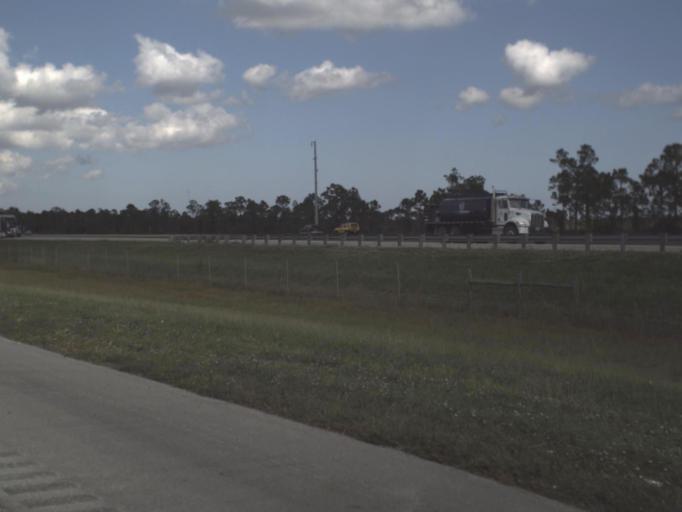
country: US
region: Florida
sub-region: Palm Beach County
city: Limestone Creek
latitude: 26.9615
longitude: -80.1707
